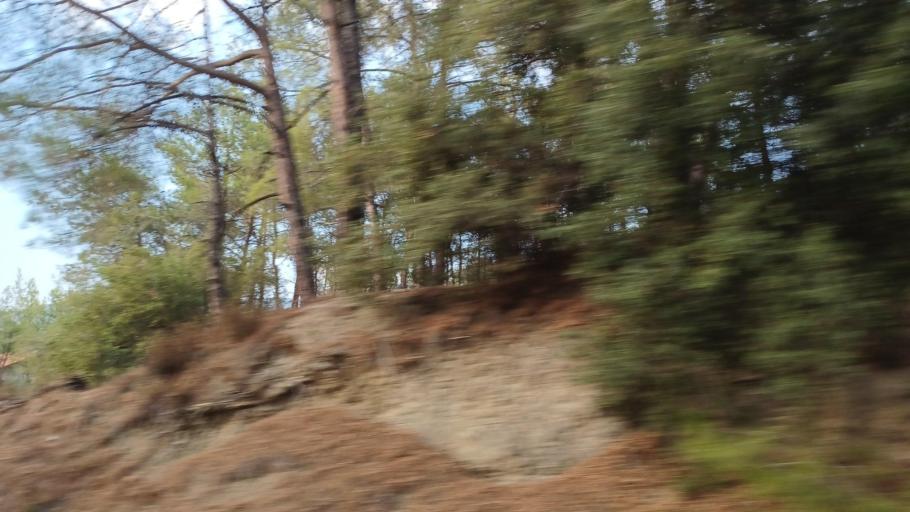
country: CY
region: Limassol
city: Pelendri
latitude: 34.8571
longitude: 32.9135
